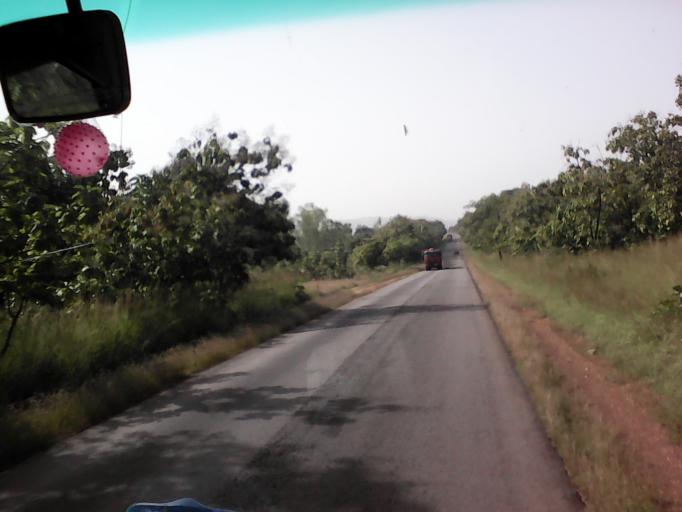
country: TG
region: Centrale
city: Sokode
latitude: 9.1159
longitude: 1.1454
